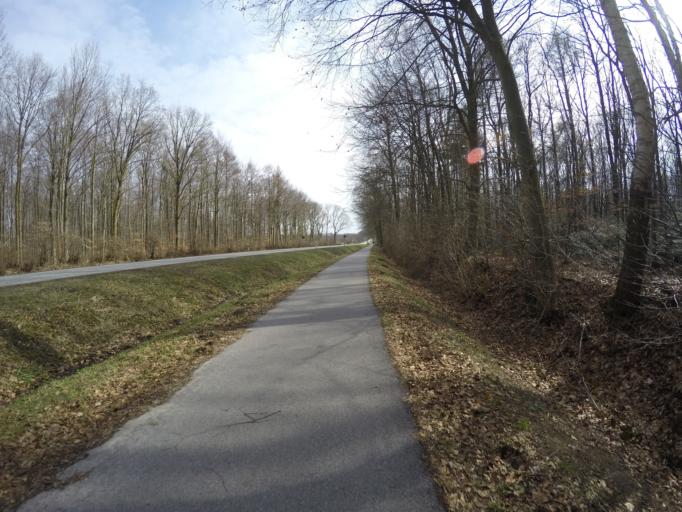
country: DE
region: Schleswig-Holstein
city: Bilsen
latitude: 53.7515
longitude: 9.8838
